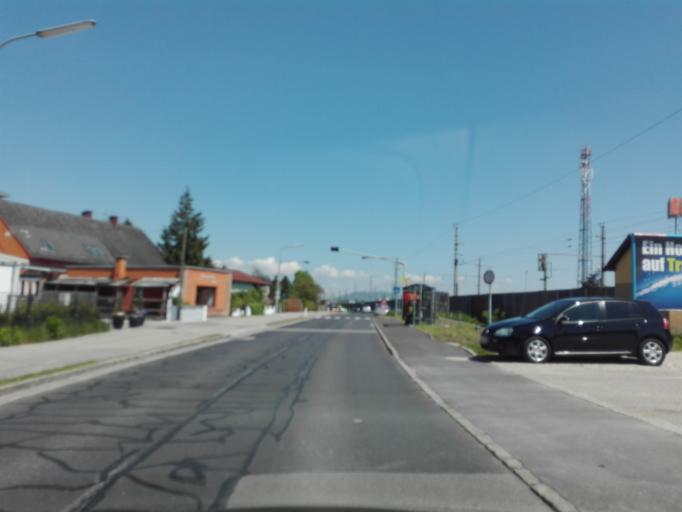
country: AT
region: Upper Austria
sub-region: Politischer Bezirk Linz-Land
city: Traun
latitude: 48.2271
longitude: 14.2548
